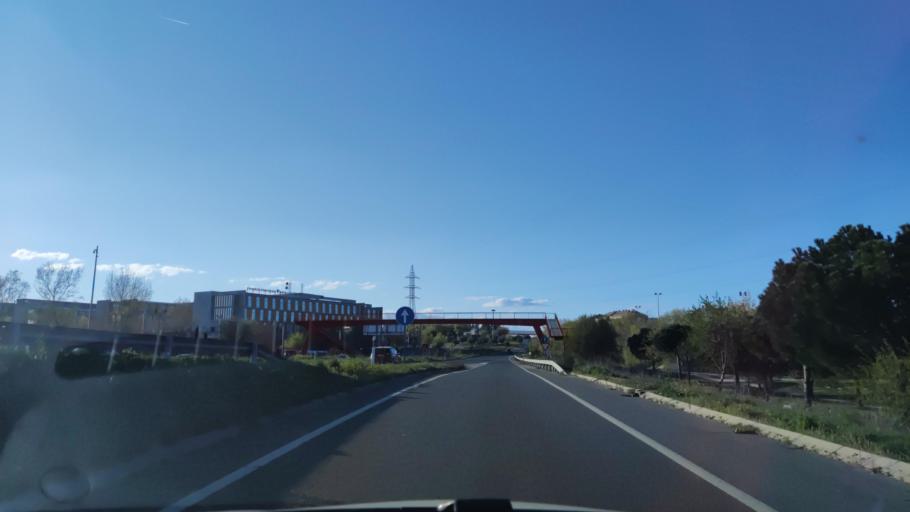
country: ES
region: Madrid
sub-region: Provincia de Madrid
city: Latina
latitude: 40.4014
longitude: -3.7798
